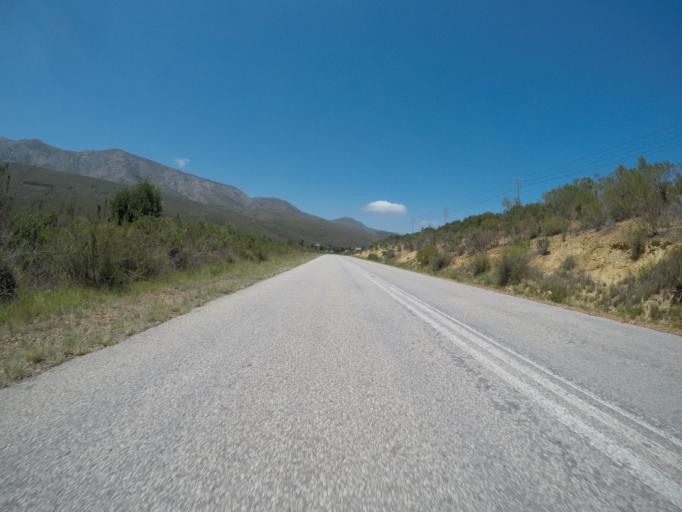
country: ZA
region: Eastern Cape
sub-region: Cacadu District Municipality
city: Kareedouw
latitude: -33.9134
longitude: 24.1830
